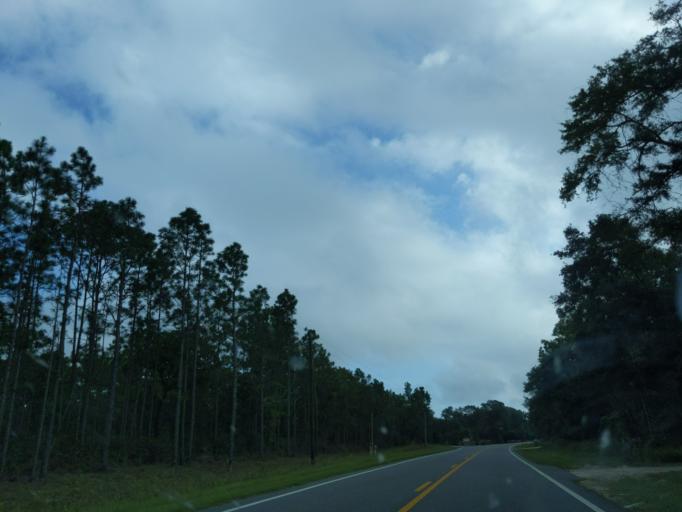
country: US
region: Florida
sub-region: Wakulla County
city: Crawfordville
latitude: 30.1231
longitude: -84.3151
